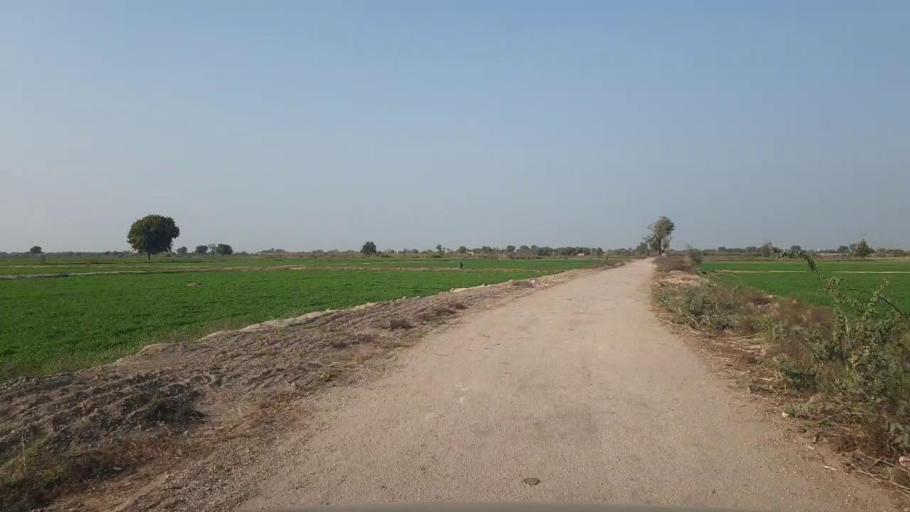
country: PK
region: Sindh
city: Hala
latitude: 25.8543
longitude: 68.3565
